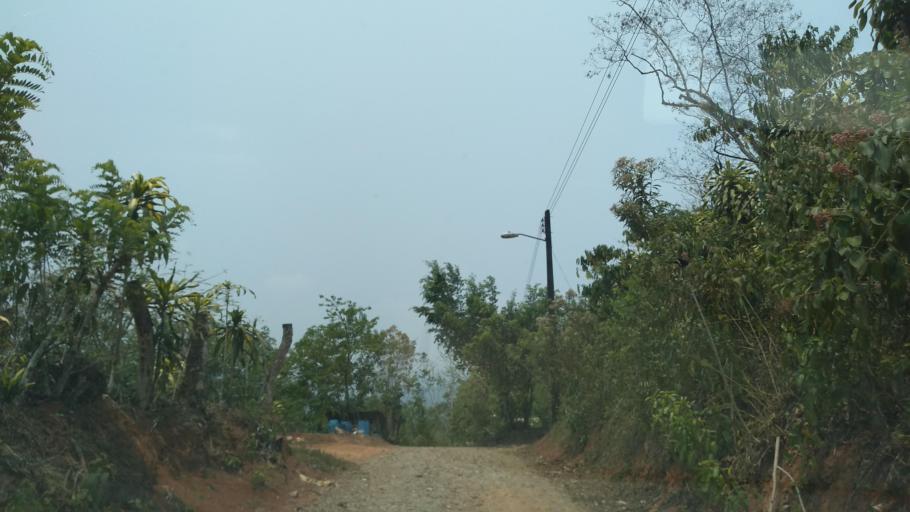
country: MX
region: Puebla
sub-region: San Sebastian Tlacotepec
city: San Martin Mazateopan
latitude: 18.4922
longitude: -96.7822
